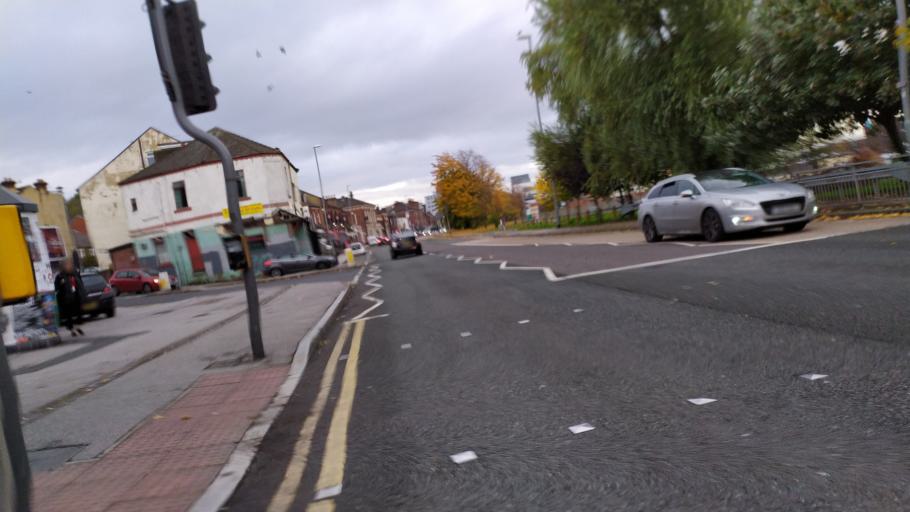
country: GB
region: England
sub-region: City and Borough of Leeds
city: Leeds
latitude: 53.8052
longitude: -1.5706
